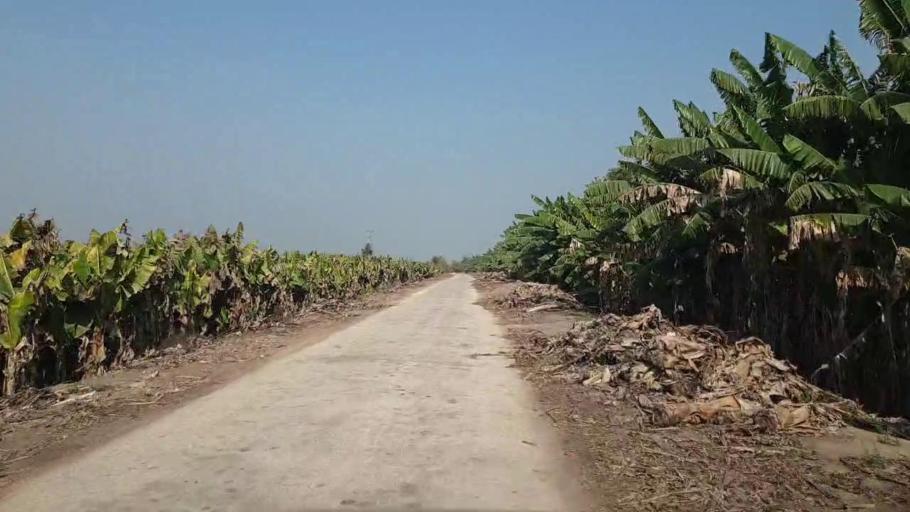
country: PK
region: Sindh
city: Bhit Shah
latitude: 25.7644
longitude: 68.4946
